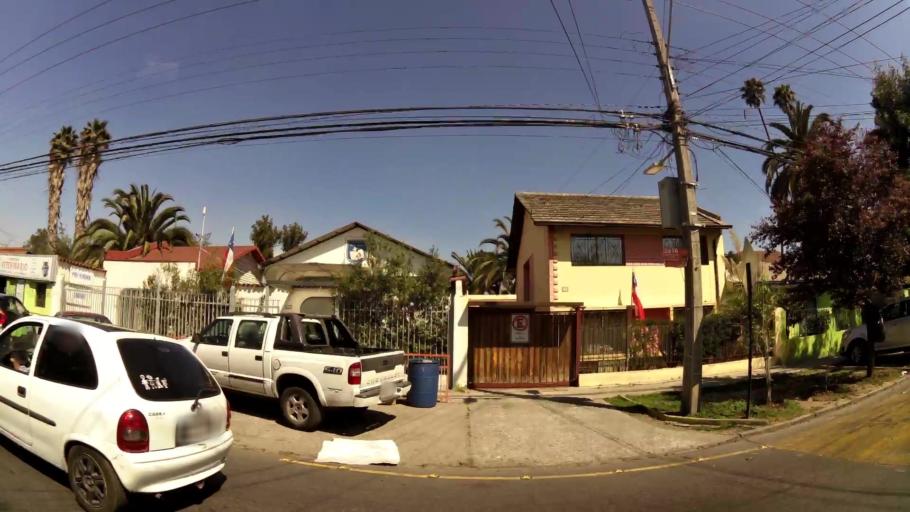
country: CL
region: Santiago Metropolitan
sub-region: Provincia de Santiago
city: Santiago
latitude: -33.5214
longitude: -70.6557
